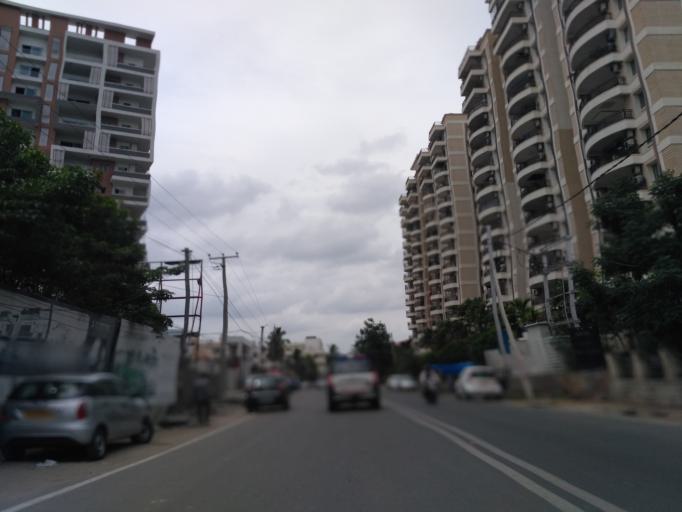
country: IN
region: Telangana
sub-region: Rangareddi
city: Kukatpalli
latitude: 17.4384
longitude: 78.3888
